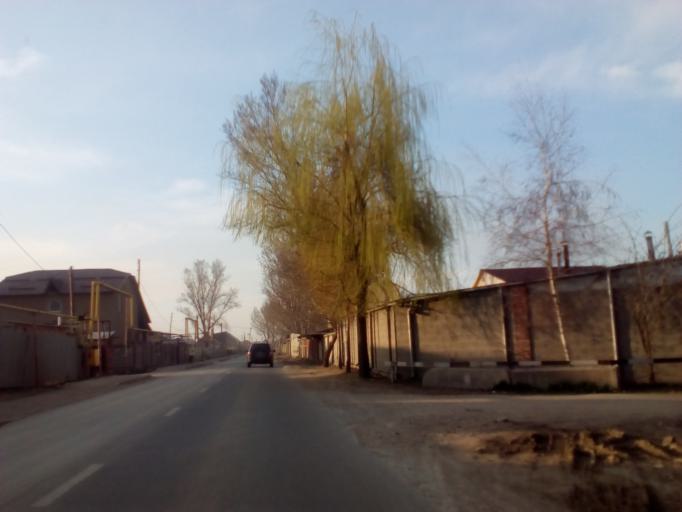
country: KZ
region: Almaty Oblysy
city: Burunday
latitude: 43.2430
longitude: 76.7877
